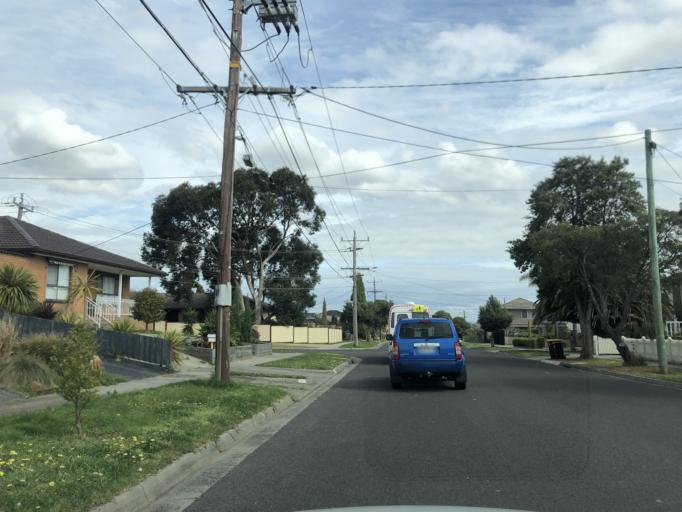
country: AU
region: Victoria
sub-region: Greater Dandenong
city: Noble Park North
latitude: -37.9525
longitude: 145.1995
